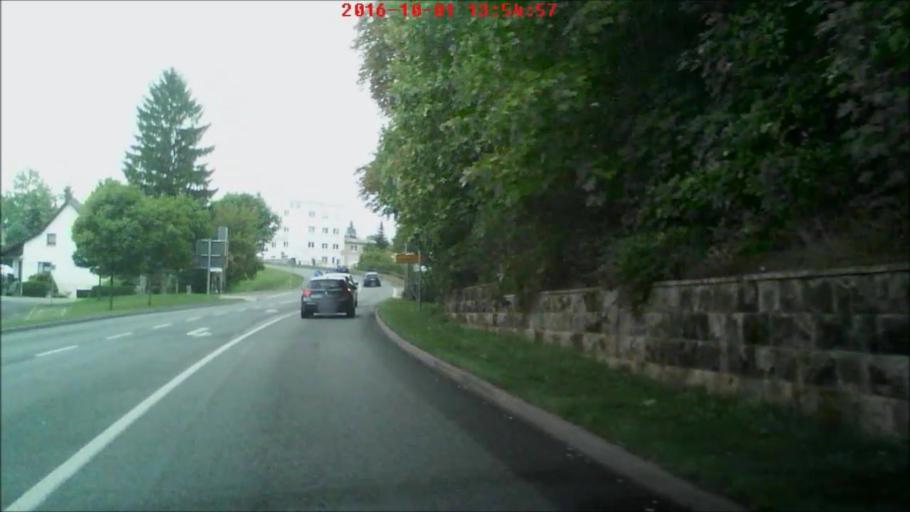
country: DE
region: Thuringia
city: Mellingen
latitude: 50.9389
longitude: 11.3958
